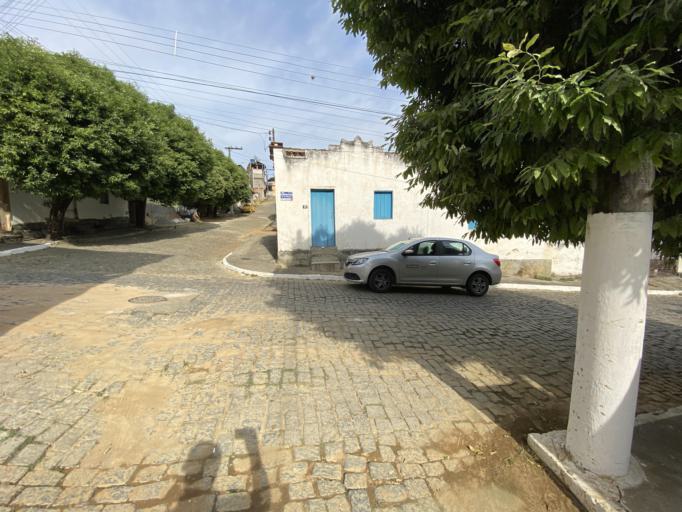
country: BR
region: Espirito Santo
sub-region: Jeronimo Monteiro
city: Jeronimo Monteiro
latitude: -20.7931
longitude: -41.3981
